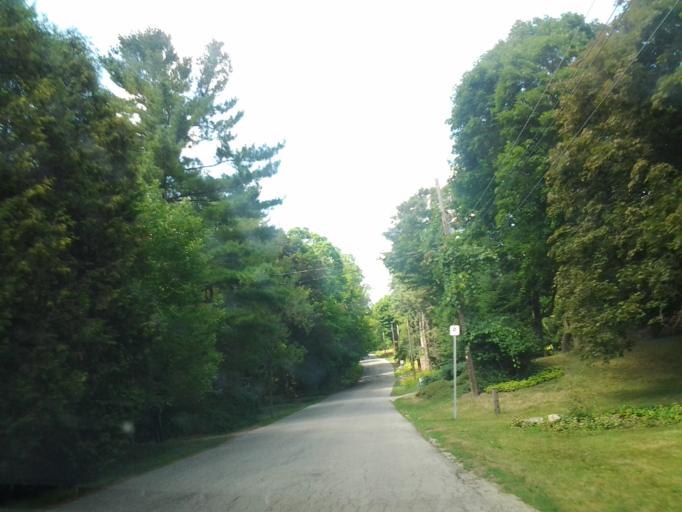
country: CA
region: Ontario
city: Ancaster
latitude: 43.2773
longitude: -79.9859
